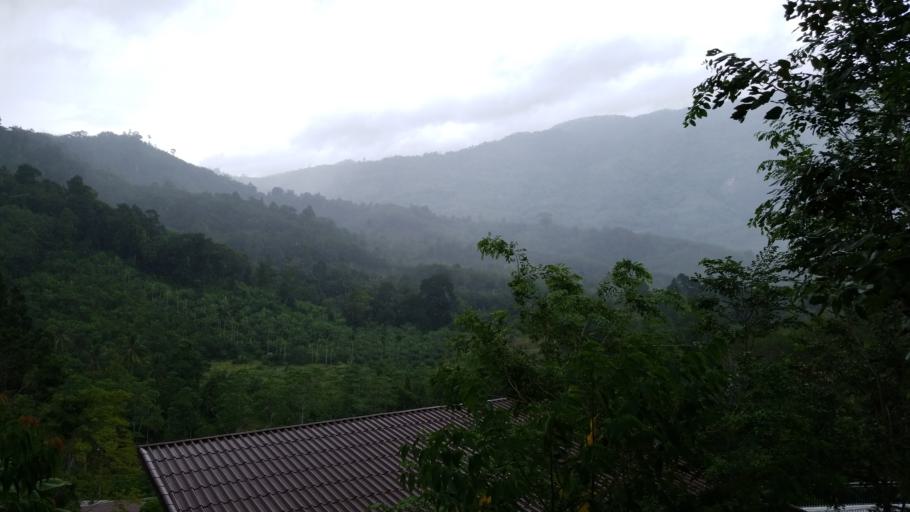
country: TH
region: Nakhon Si Thammarat
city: Lan Saka
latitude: 8.3479
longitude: 99.7267
